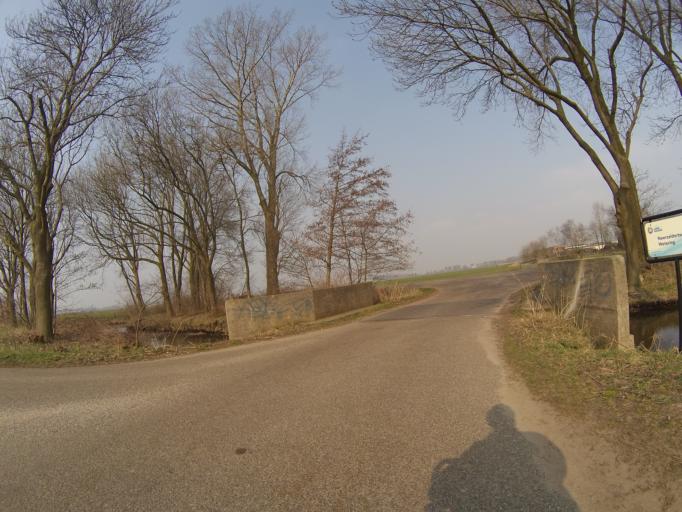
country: NL
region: Utrecht
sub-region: Gemeente Baarn
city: Baarn
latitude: 52.2029
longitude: 5.3309
